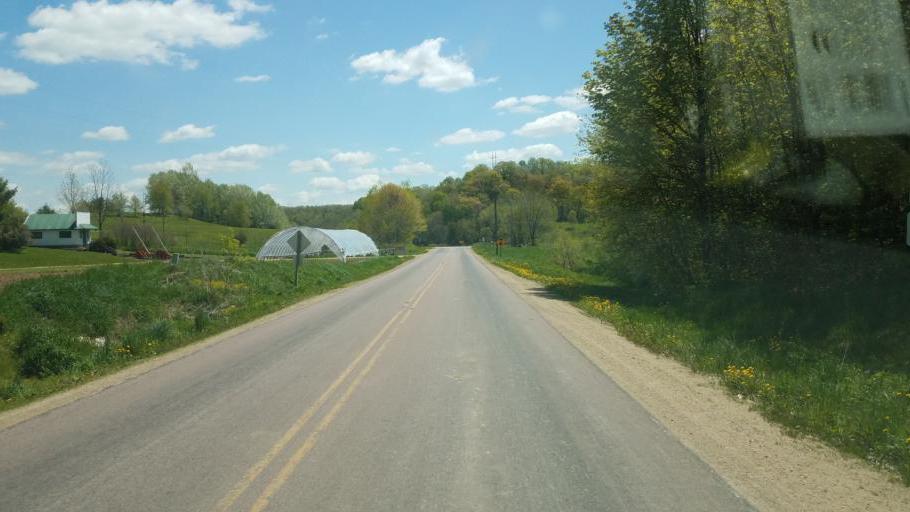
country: US
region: Wisconsin
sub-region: Vernon County
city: Hillsboro
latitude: 43.6456
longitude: -90.4390
